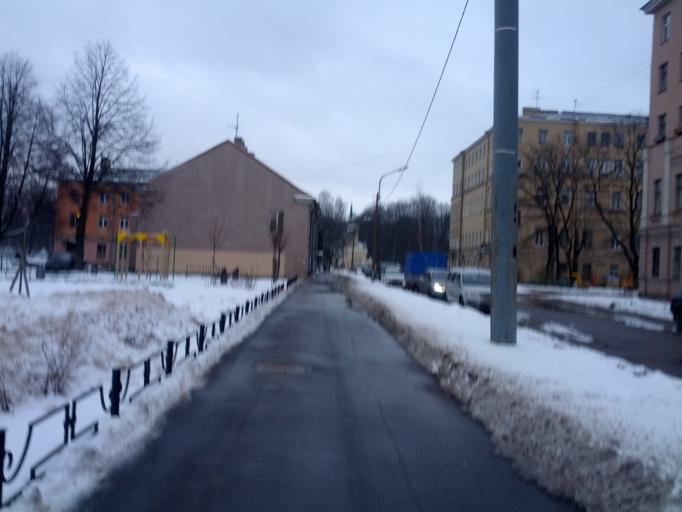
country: RU
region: St.-Petersburg
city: Centralniy
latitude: 59.9054
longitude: 30.3551
